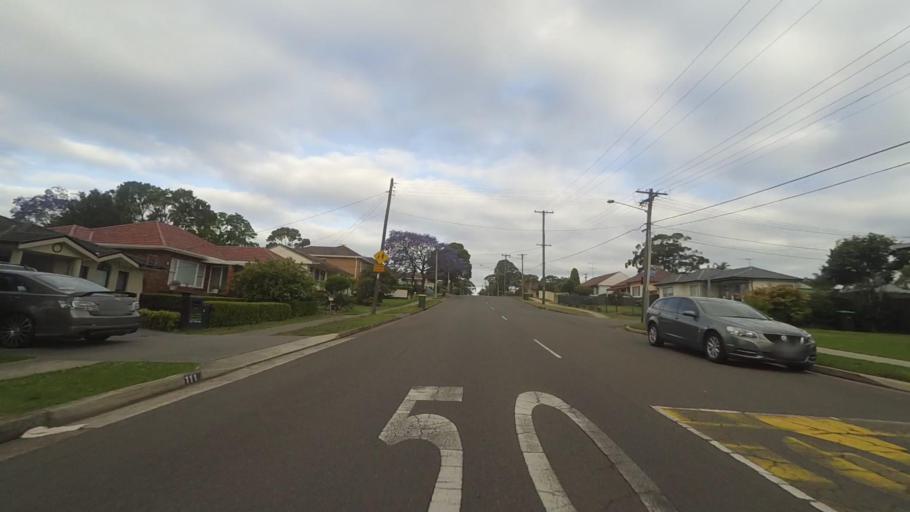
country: AU
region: New South Wales
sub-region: Sutherland Shire
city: Engadine
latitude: -34.0598
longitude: 151.0064
